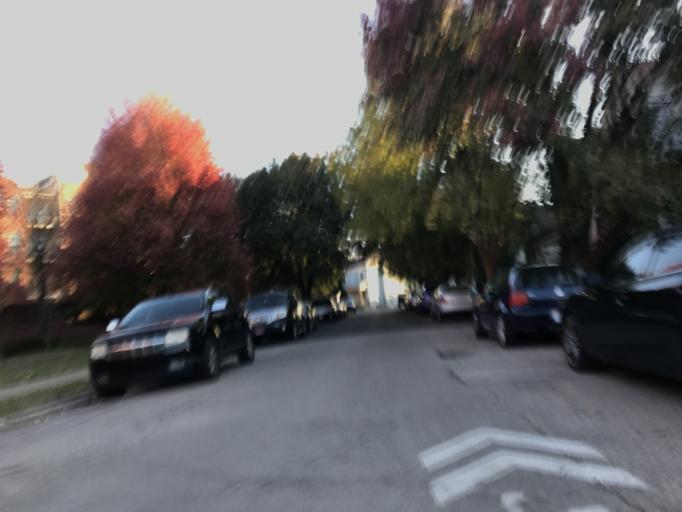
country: US
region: Kentucky
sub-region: Jefferson County
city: Louisville
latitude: 38.2427
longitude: -85.7307
